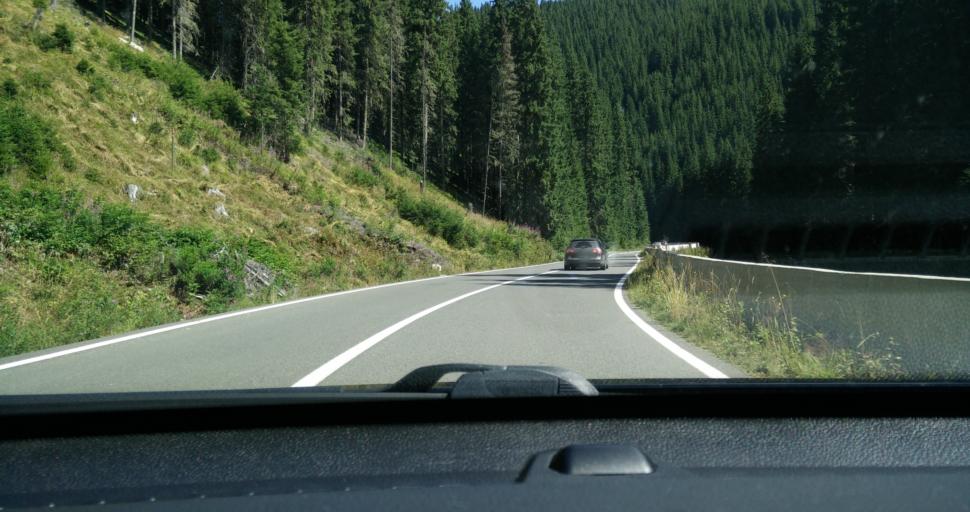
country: RO
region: Hunedoara
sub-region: Oras Petrila
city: Petrila
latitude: 45.5174
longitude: 23.6505
